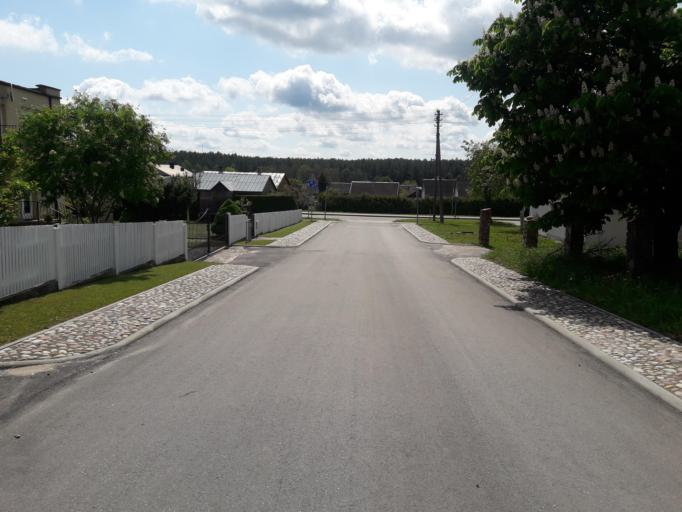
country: LT
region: Alytaus apskritis
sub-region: Alytaus rajonas
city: Daugai
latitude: 54.1664
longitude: 24.1939
